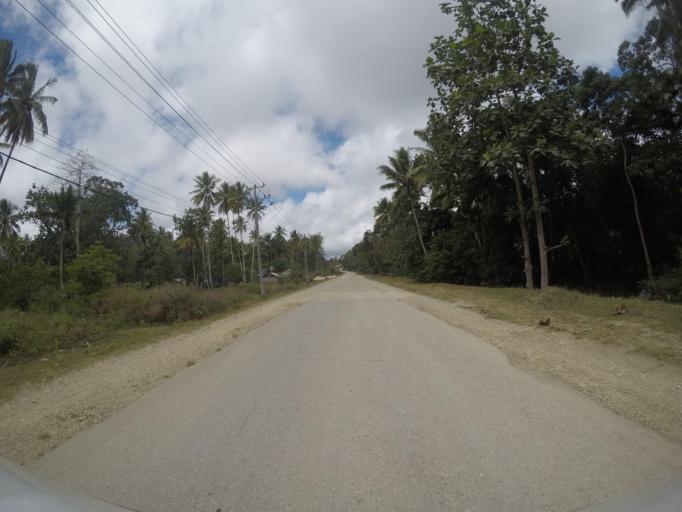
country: TL
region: Lautem
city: Lospalos
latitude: -8.5192
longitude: 126.9930
